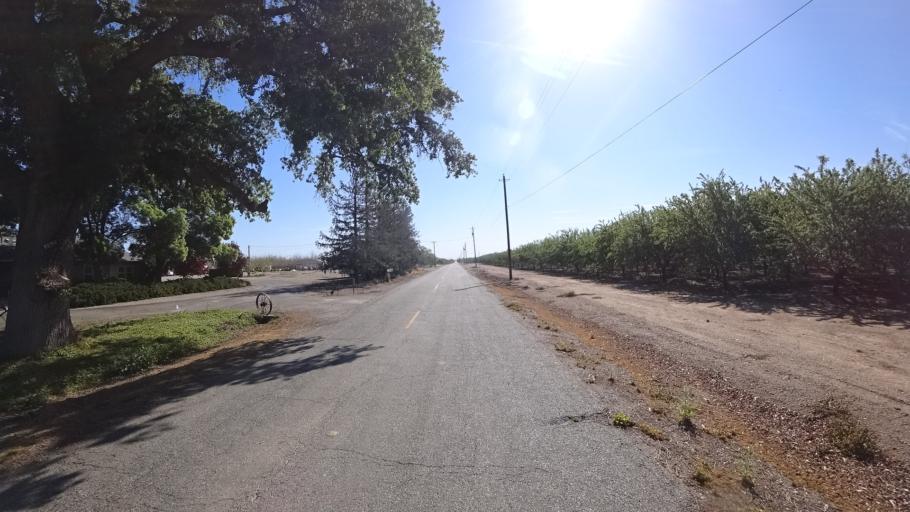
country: US
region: California
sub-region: Glenn County
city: Willows
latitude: 39.6113
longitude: -122.1864
